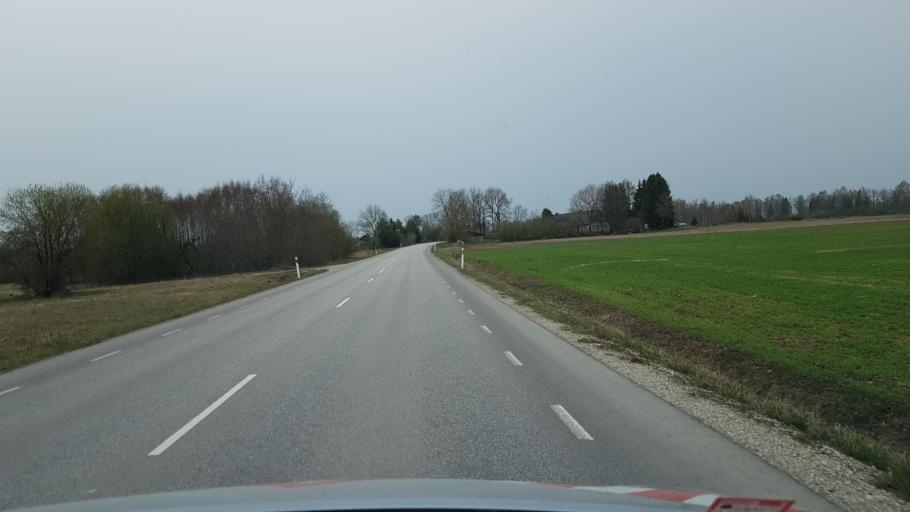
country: EE
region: Harju
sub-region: Raasiku vald
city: Arukula
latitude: 59.3776
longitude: 25.0130
